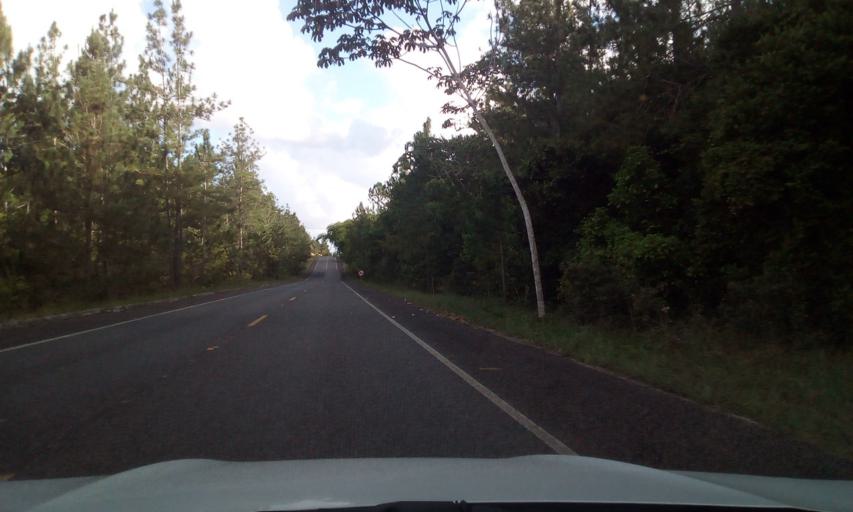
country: BR
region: Bahia
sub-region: Entre Rios
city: Entre Rios
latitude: -12.1177
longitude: -37.7876
